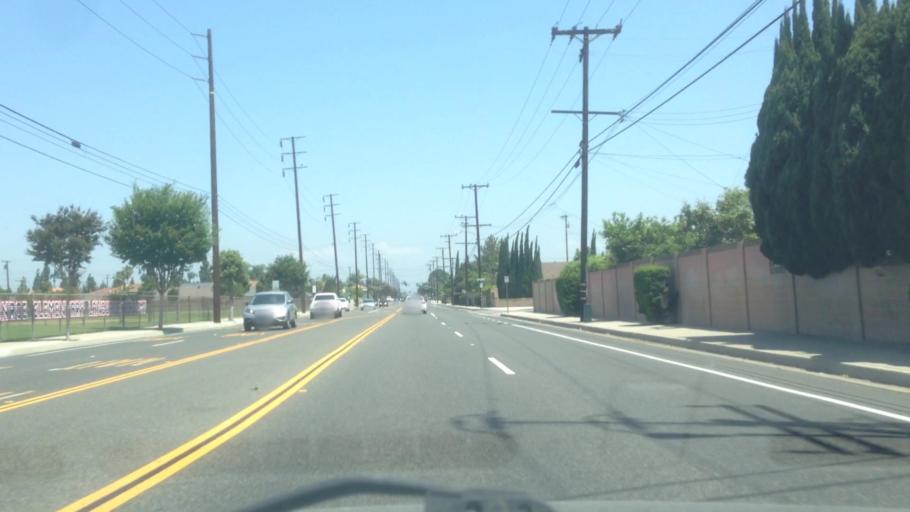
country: US
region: California
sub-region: Orange County
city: Fountain Valley
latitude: 33.7275
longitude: -117.9285
